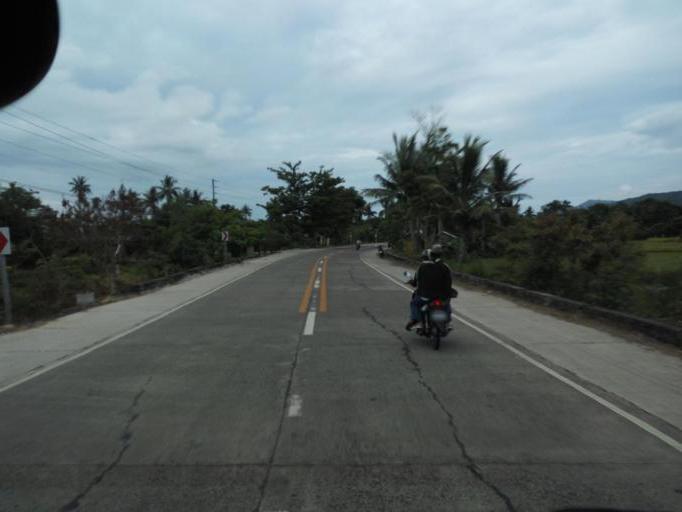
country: PH
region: Cagayan Valley
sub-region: Province of Cagayan
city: Cabiraoan
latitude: 18.3428
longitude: 122.0762
